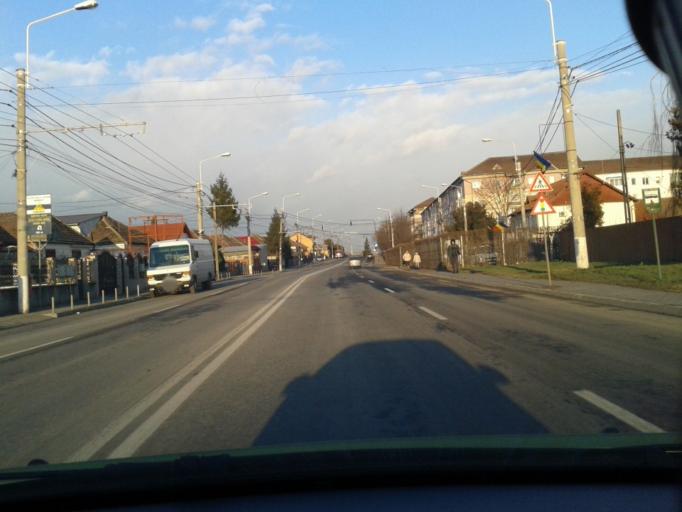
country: RO
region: Sibiu
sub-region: Municipiul Medias
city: Medias
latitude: 46.1485
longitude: 24.3269
